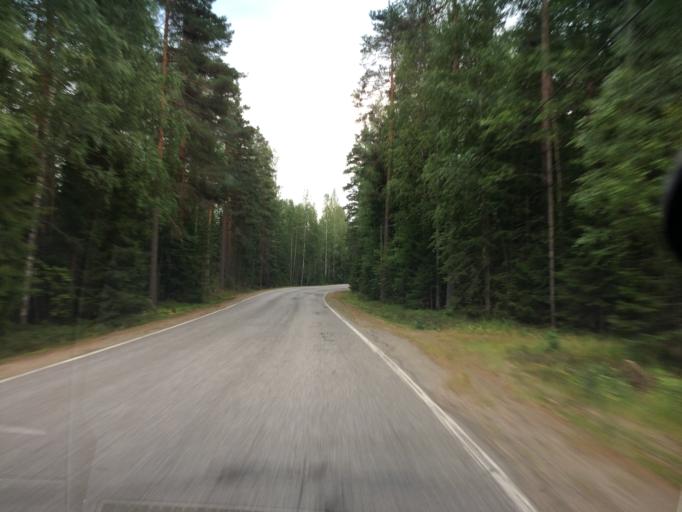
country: FI
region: Haeme
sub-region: Haemeenlinna
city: Tuulos
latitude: 61.2334
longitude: 24.7107
